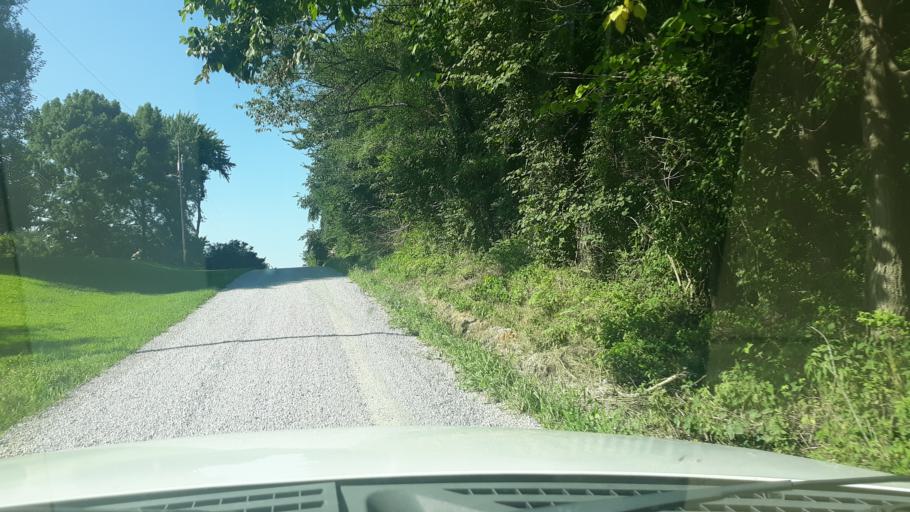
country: US
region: Illinois
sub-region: Saline County
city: Eldorado
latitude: 37.8427
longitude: -88.4937
